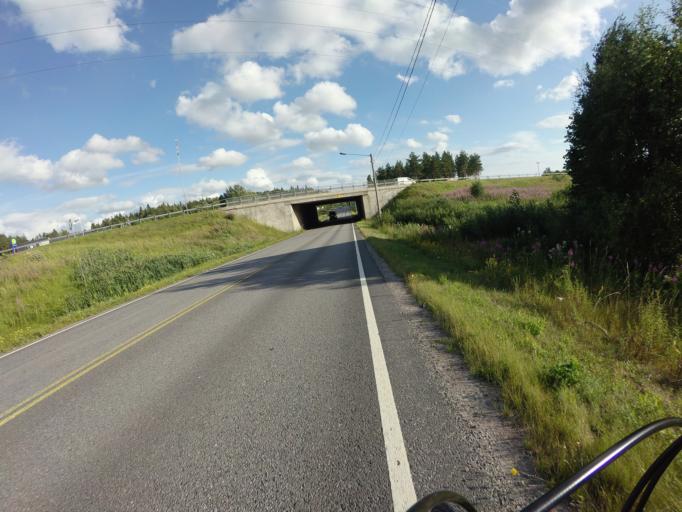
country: FI
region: Varsinais-Suomi
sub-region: Turku
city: Vahto
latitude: 60.5442
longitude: 22.3402
